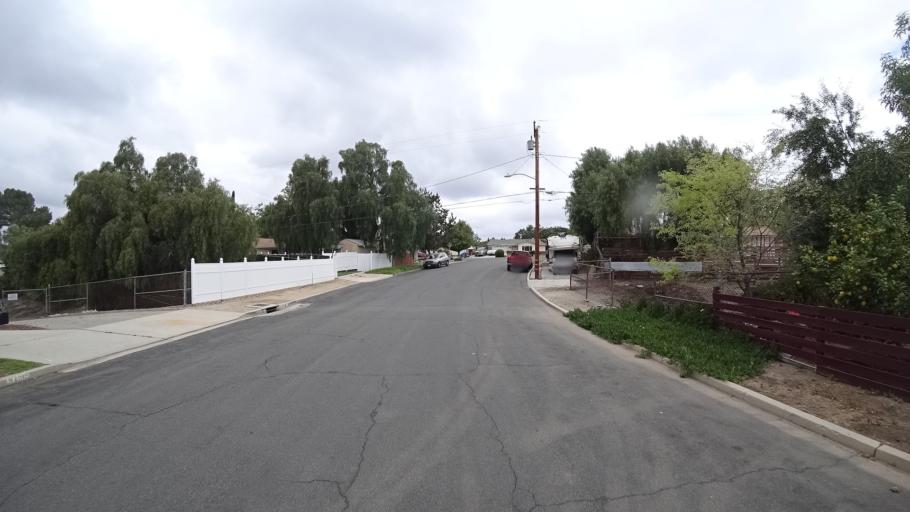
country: US
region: California
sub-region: Ventura County
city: Thousand Oaks
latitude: 34.2098
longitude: -118.8539
